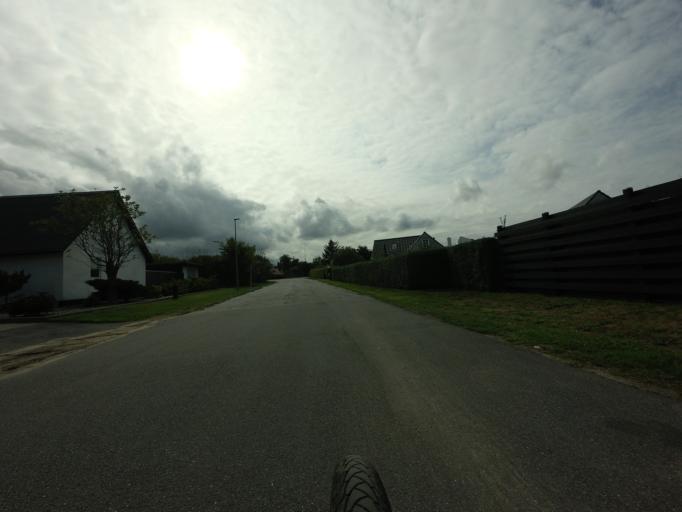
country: DK
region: North Denmark
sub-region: Hjorring Kommune
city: Hjorring
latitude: 57.4867
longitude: 9.9937
